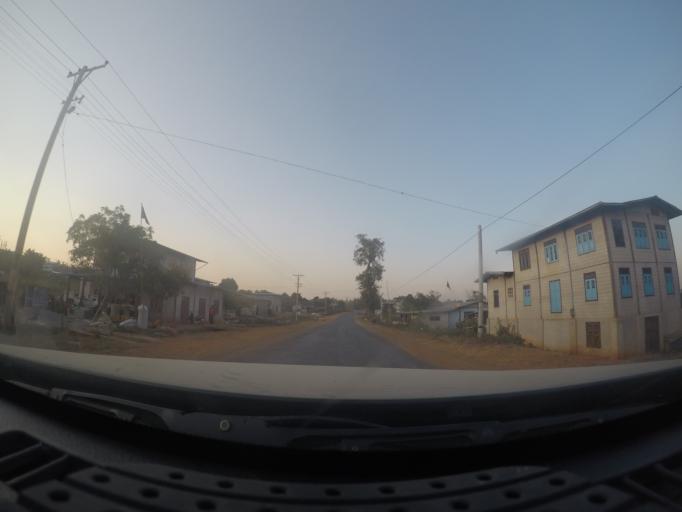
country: MM
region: Shan
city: Taunggyi
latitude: 20.5657
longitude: 97.0630
